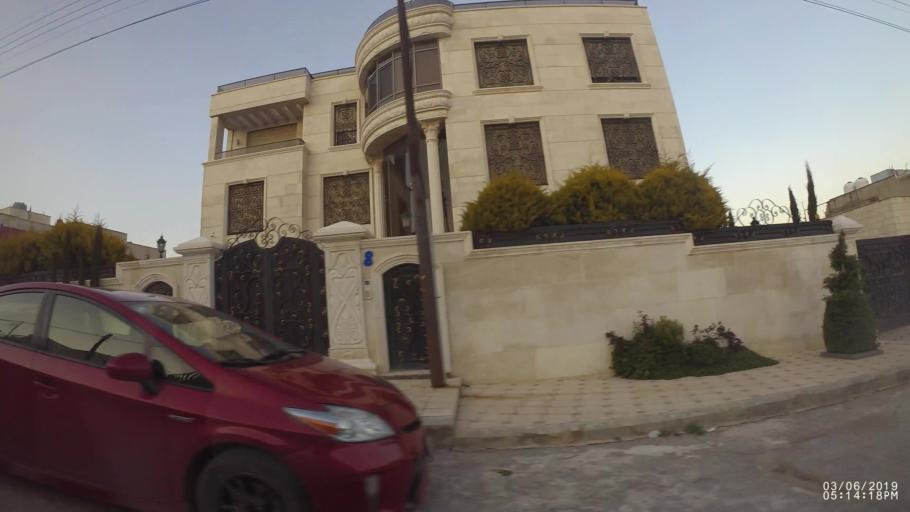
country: JO
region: Amman
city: Amman
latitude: 31.9934
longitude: 35.9501
